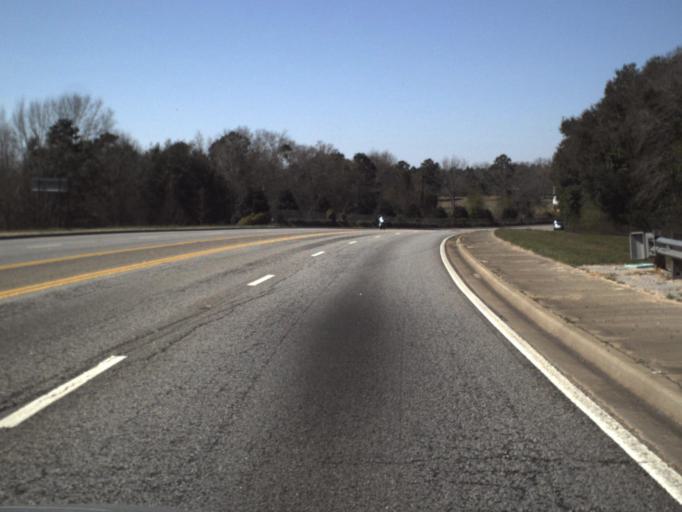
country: US
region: Florida
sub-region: Jackson County
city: Graceville
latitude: 30.9462
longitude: -85.3989
